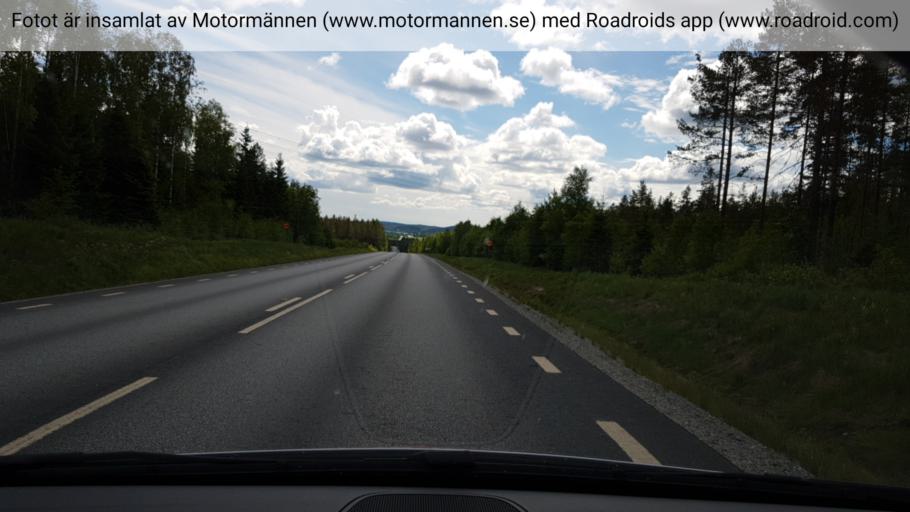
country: SE
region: Vaesterbotten
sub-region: Vannas Kommun
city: Vannasby
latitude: 64.0461
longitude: 20.0010
